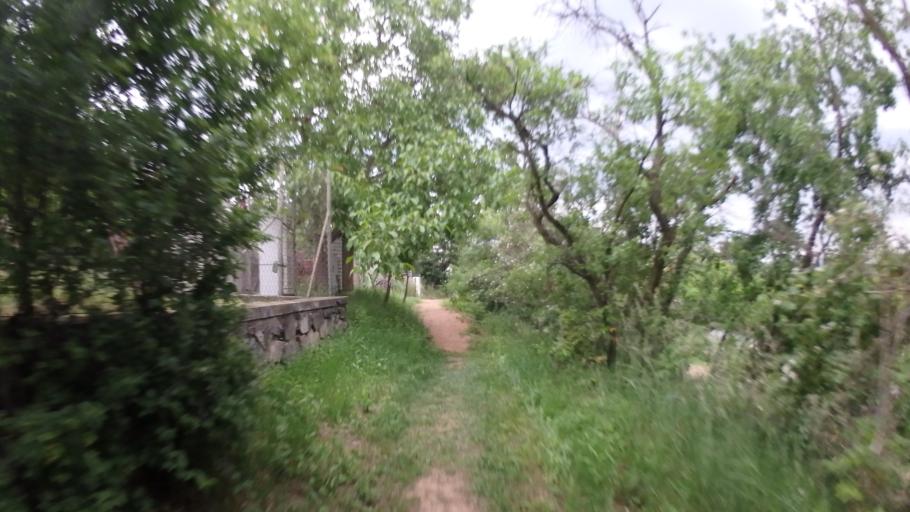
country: CZ
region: South Moravian
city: Ostopovice
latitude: 49.1343
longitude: 16.5439
